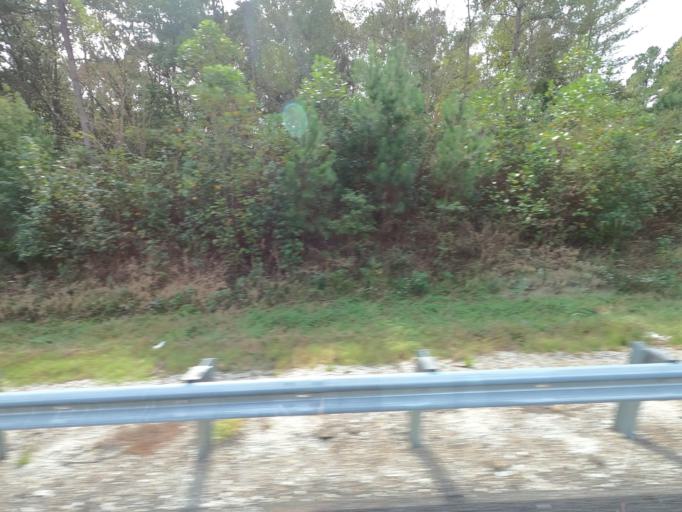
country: US
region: Tennessee
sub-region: Decatur County
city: Parsons
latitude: 35.8190
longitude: -88.2519
